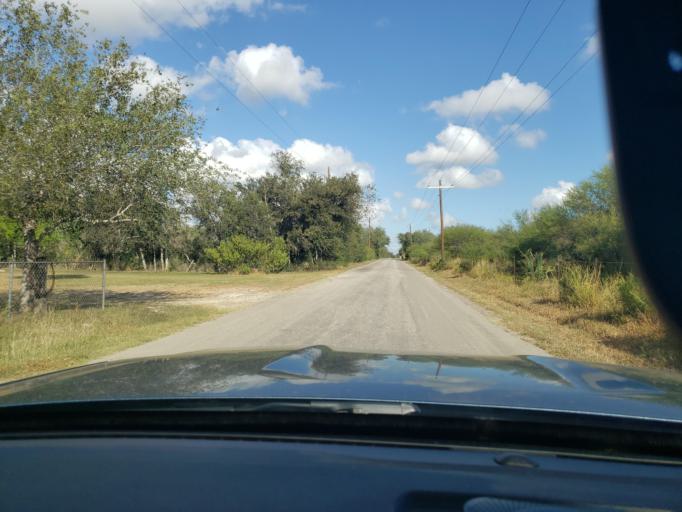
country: US
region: Texas
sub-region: Bee County
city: Beeville
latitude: 28.4427
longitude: -97.7142
